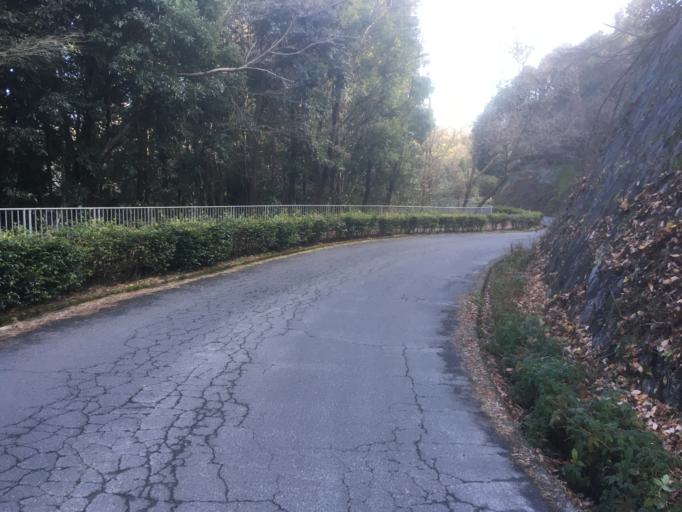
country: JP
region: Nara
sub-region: Ikoma-shi
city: Ikoma
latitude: 34.6989
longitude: 135.6749
